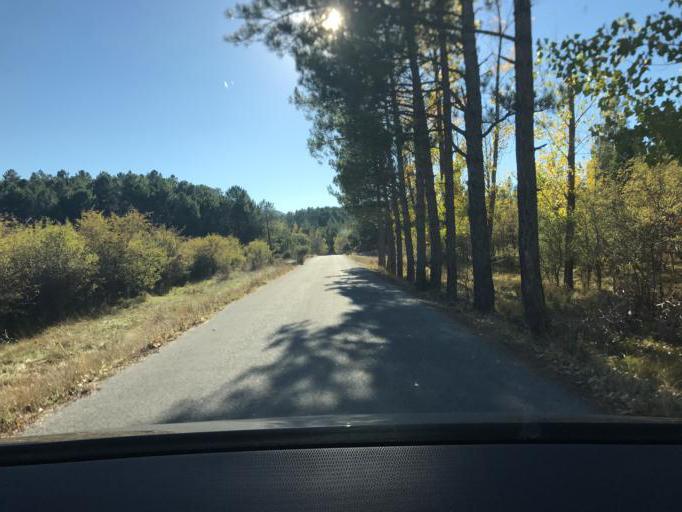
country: ES
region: Andalusia
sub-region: Provincia de Granada
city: Beas de Granada
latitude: 37.3046
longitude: -3.4661
